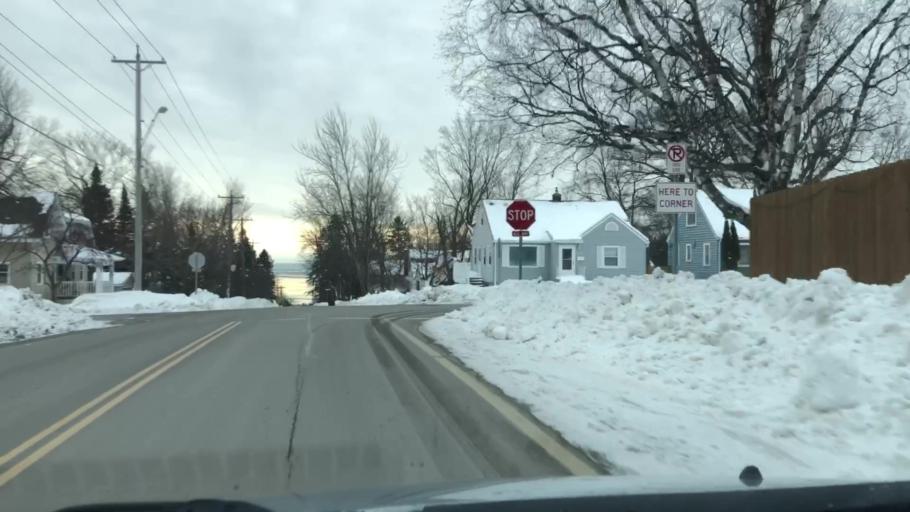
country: US
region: Minnesota
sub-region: Saint Louis County
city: Arnold
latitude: 46.8342
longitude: -92.0638
